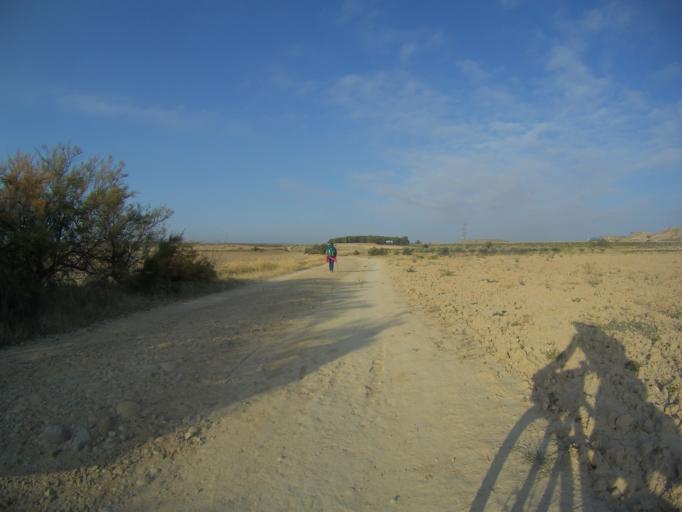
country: ES
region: Basque Country
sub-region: Provincia de Alava
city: Moreda de Alava
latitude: 42.4952
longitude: -2.3980
